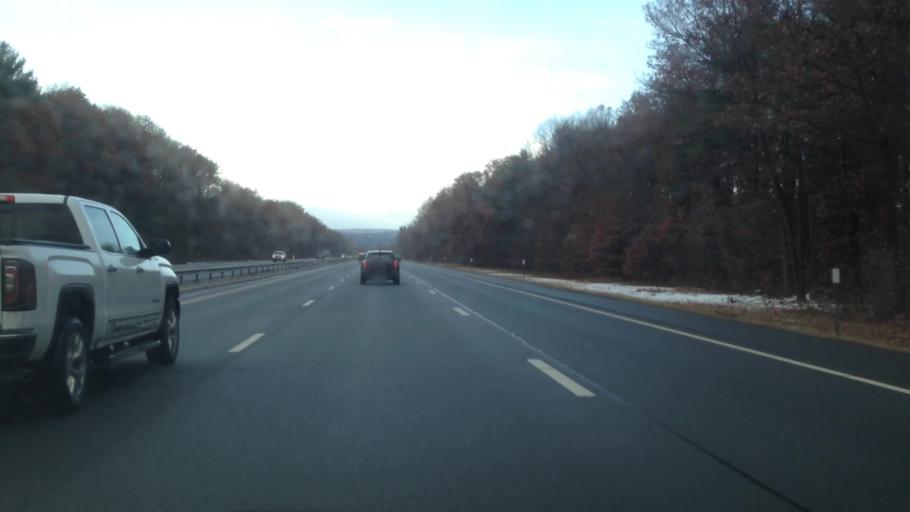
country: US
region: New York
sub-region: Schenectady County
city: Rotterdam
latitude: 42.7679
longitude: -73.9637
